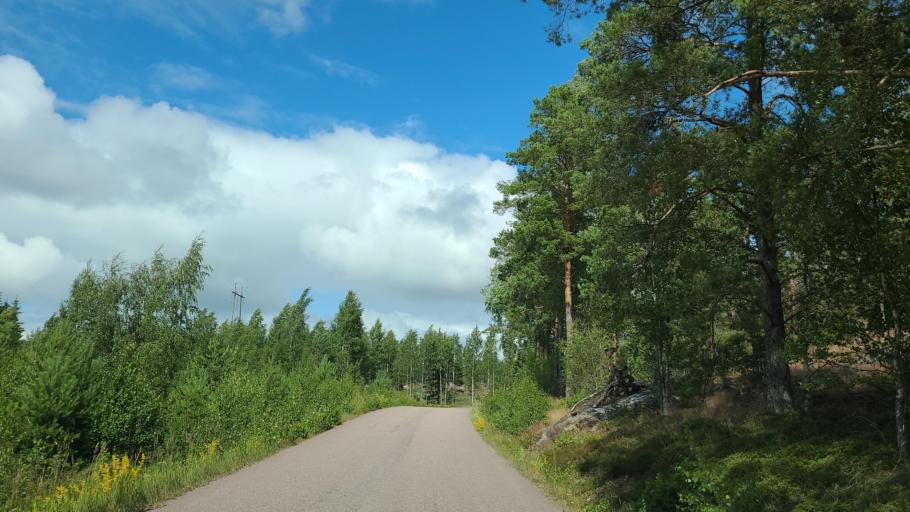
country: FI
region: Varsinais-Suomi
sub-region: Aboland-Turunmaa
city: Nagu
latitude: 60.1759
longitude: 22.0430
